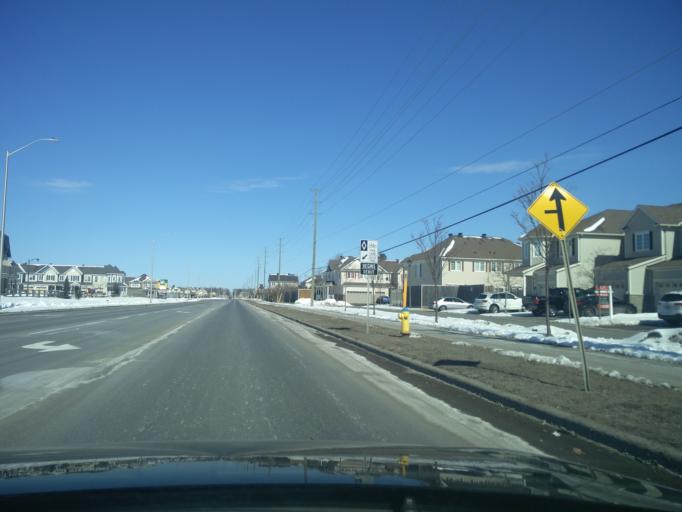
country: CA
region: Ontario
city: Bells Corners
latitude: 45.2471
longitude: -75.7322
